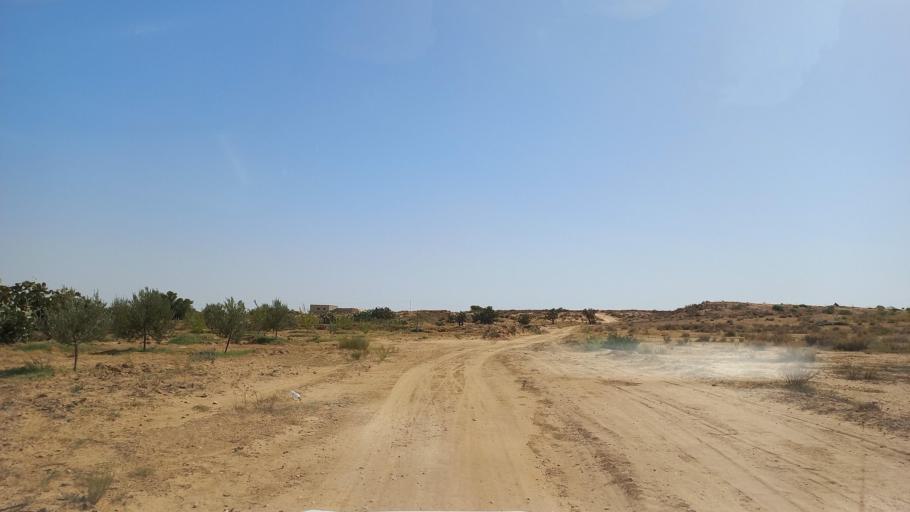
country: TN
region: Al Qasrayn
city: Kasserine
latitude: 35.2223
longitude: 9.0359
